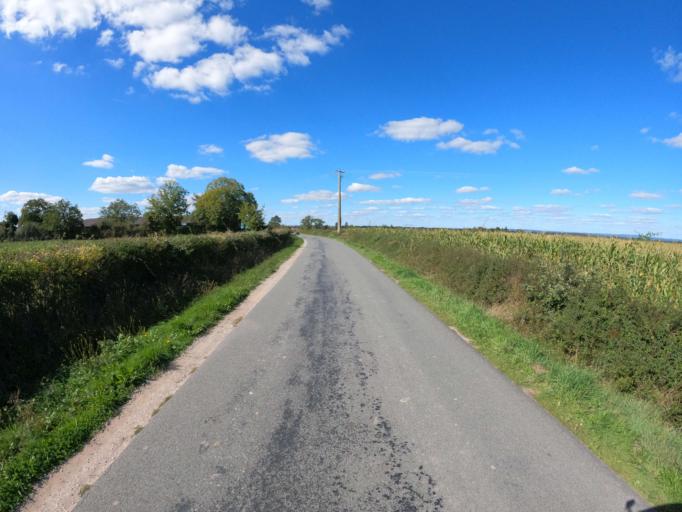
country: FR
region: Auvergne
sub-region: Departement de l'Allier
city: Doyet
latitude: 46.4040
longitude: 2.7416
